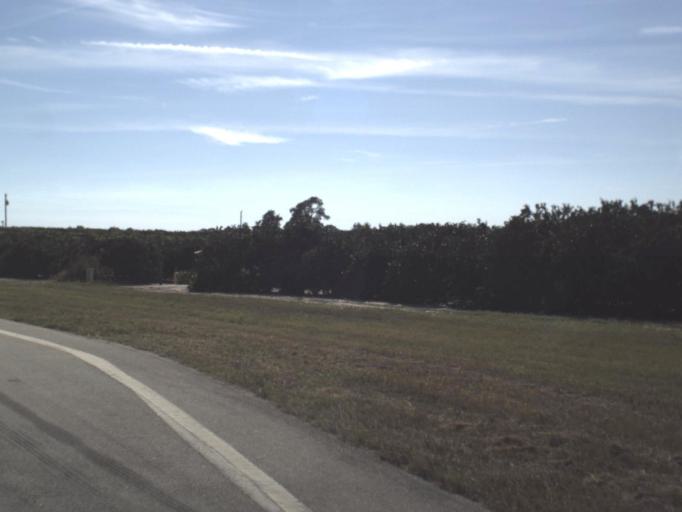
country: US
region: Florida
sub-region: Highlands County
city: Placid Lakes
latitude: 27.1366
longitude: -81.3293
